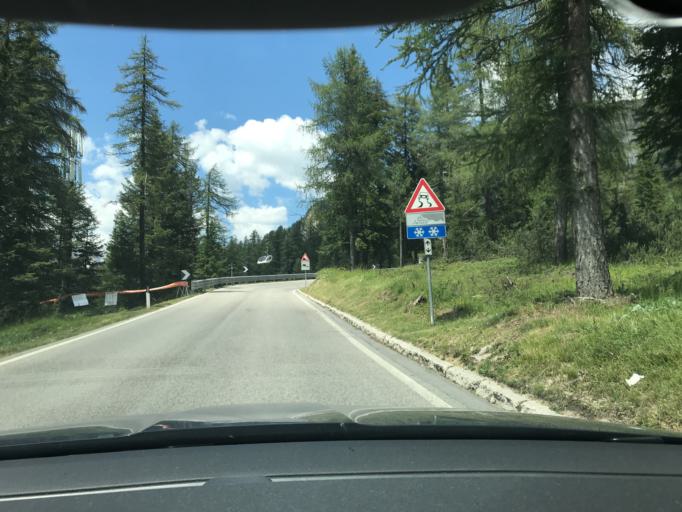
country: IT
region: Veneto
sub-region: Provincia di Belluno
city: Cortina d'Ampezzo
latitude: 46.5522
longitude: 12.1902
